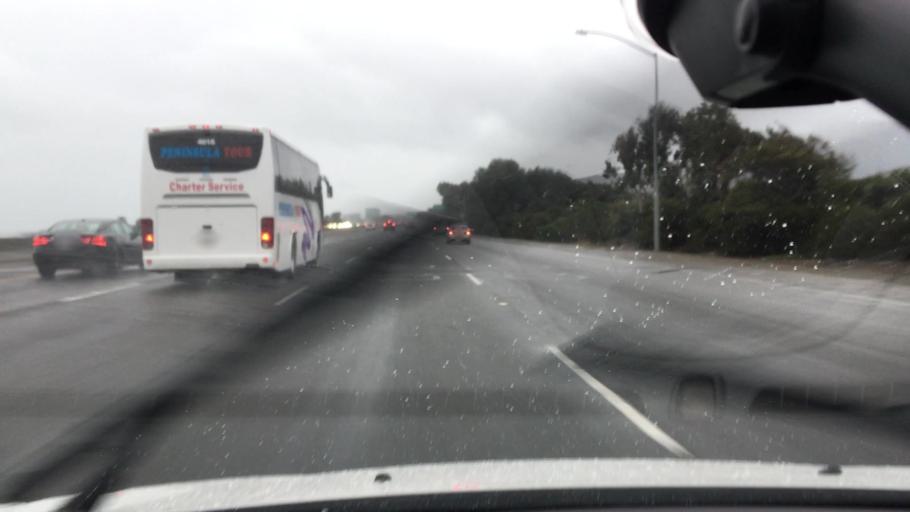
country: US
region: California
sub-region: San Mateo County
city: Brisbane
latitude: 37.7037
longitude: -122.3941
